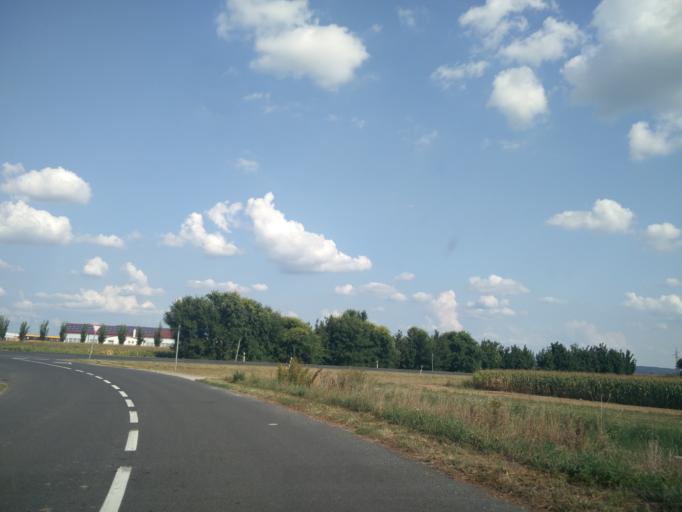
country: HU
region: Zala
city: Zalaegerszeg
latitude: 46.8790
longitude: 16.8293
